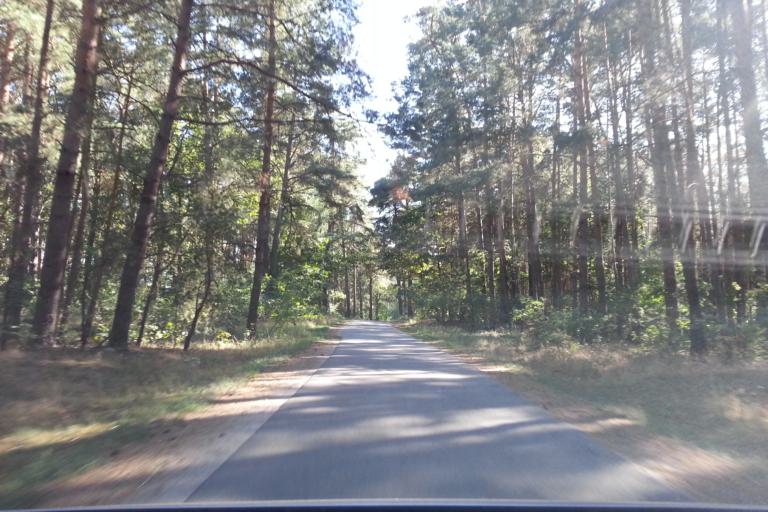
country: DE
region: Mecklenburg-Vorpommern
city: Torgelow
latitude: 53.6642
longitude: 14.0349
